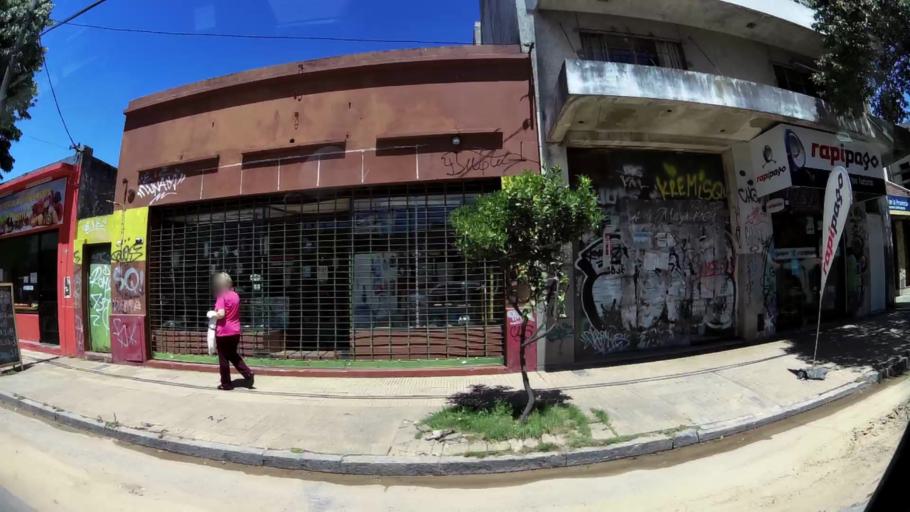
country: AR
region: Buenos Aires
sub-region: Partido de San Isidro
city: San Isidro
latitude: -34.4953
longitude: -58.5127
